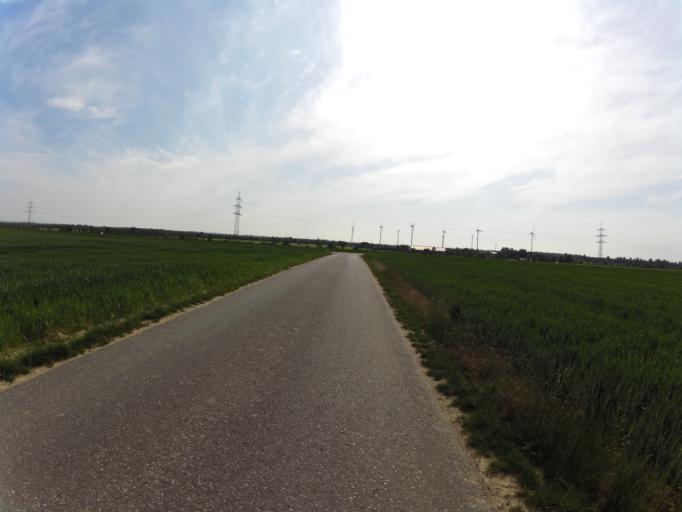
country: DE
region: North Rhine-Westphalia
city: Niedermerz
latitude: 50.8736
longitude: 6.2778
